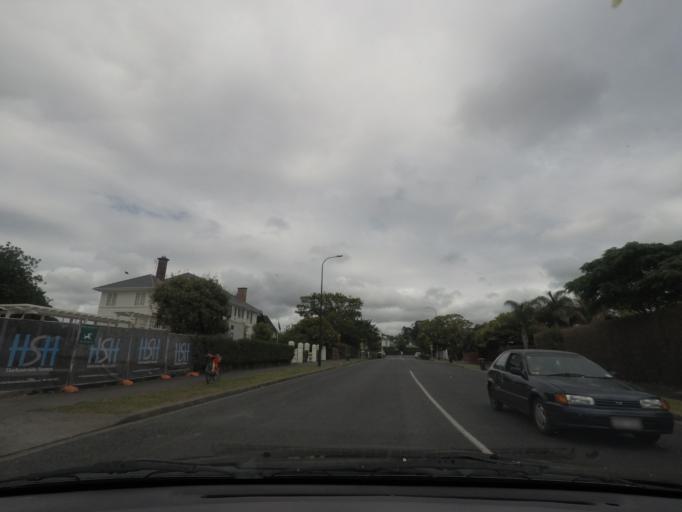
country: NZ
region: Auckland
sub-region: Auckland
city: Auckland
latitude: -36.8711
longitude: 174.7851
